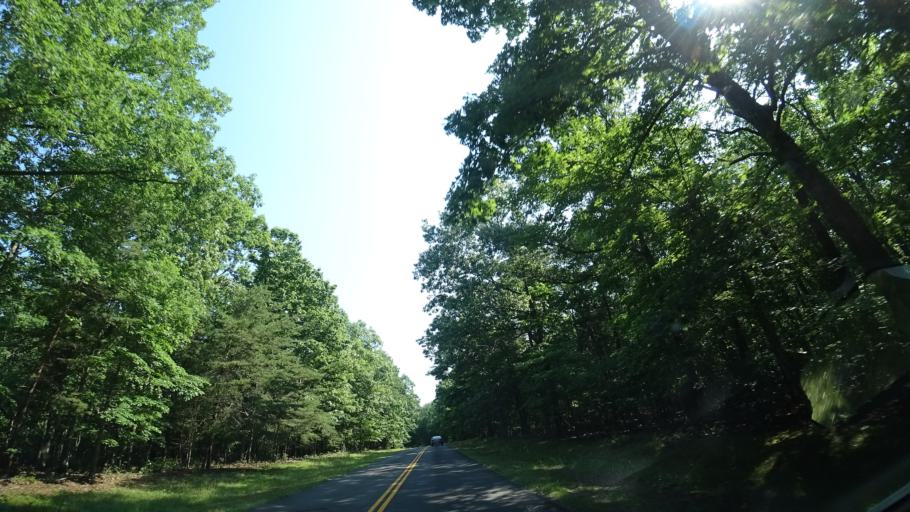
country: US
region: Virginia
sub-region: Louisa County
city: Louisa
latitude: 38.1339
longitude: -77.8181
